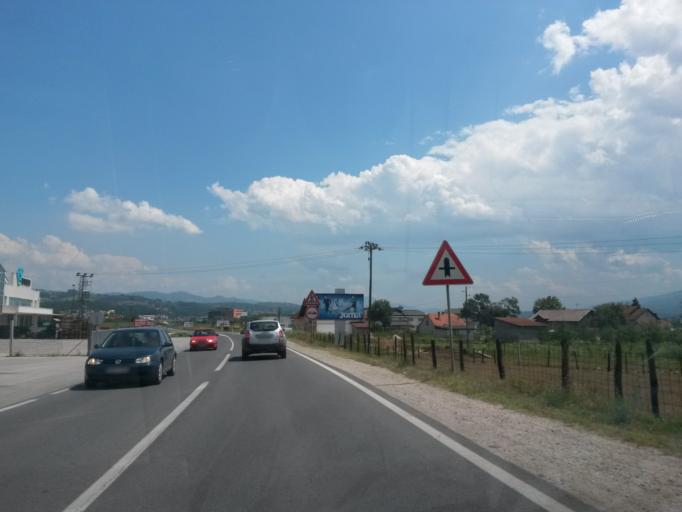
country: BA
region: Federation of Bosnia and Herzegovina
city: Vitez
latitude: 44.1707
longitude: 17.7660
